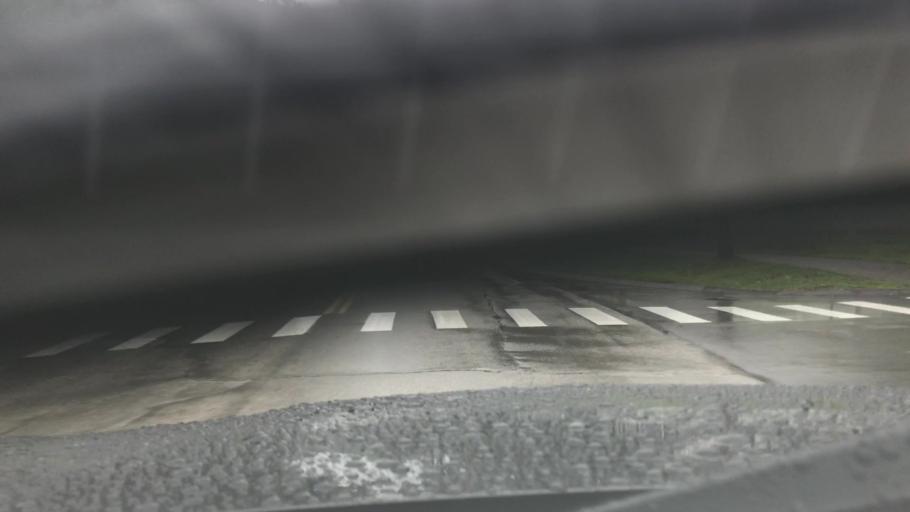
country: US
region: New Hampshire
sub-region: Strafford County
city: Durham
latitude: 43.1394
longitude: -70.9261
